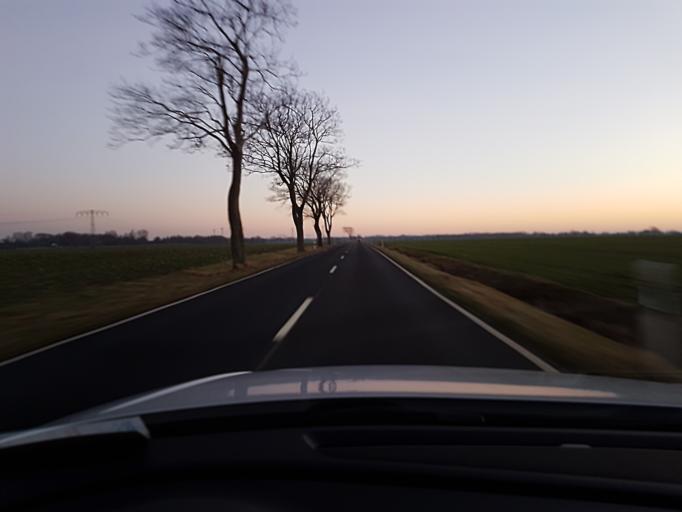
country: DE
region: Mecklenburg-Vorpommern
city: Gingst
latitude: 54.4920
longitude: 13.2842
